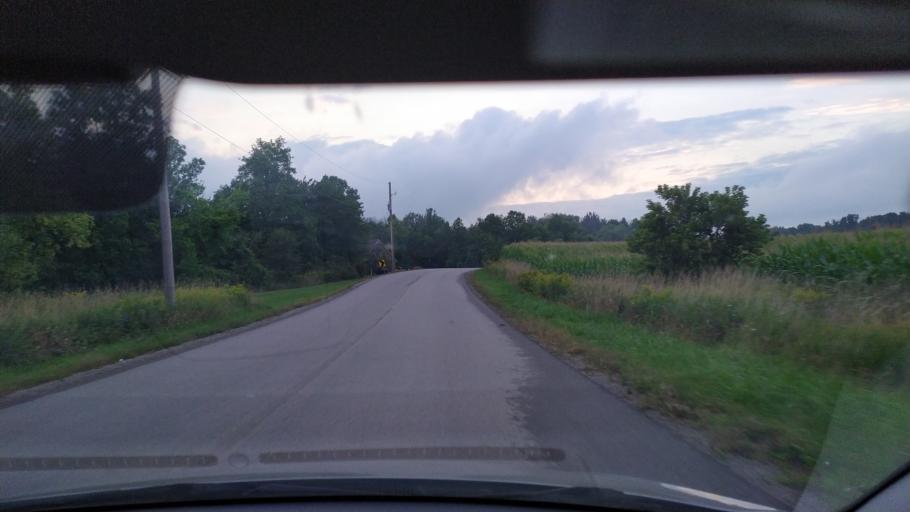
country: CA
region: Ontario
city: Kitchener
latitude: 43.3472
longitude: -80.6386
